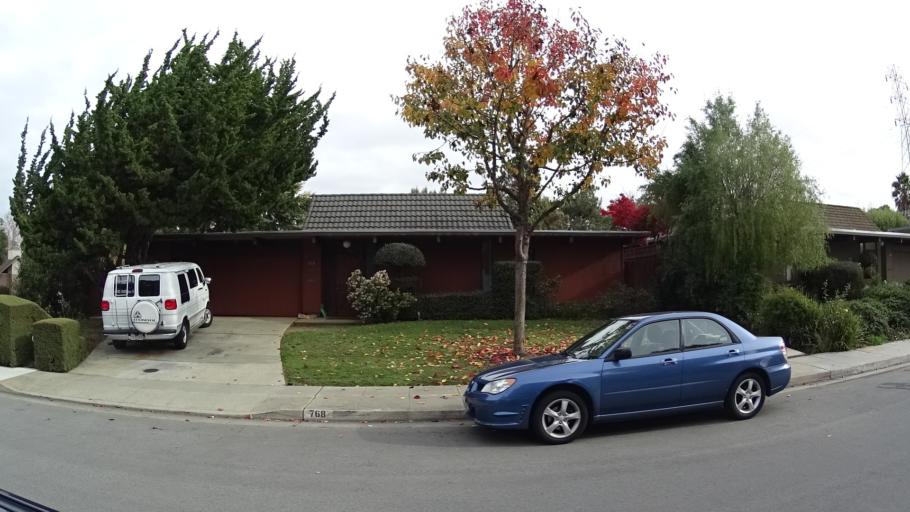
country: US
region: California
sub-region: Santa Clara County
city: Sunnyvale
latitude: 37.3686
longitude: -122.0456
